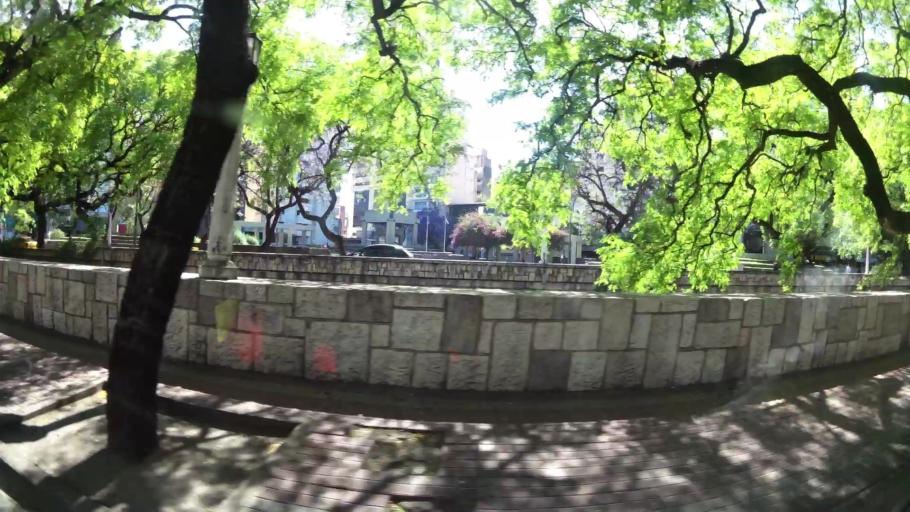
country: AR
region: Cordoba
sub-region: Departamento de Capital
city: Cordoba
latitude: -31.4160
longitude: -64.1908
